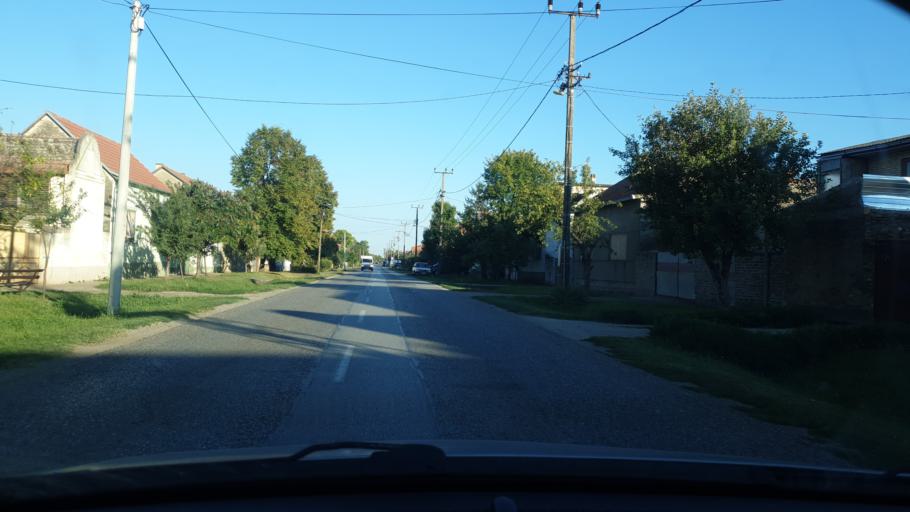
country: RS
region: Autonomna Pokrajina Vojvodina
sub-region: Sremski Okrug
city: Ruma
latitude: 44.9792
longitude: 19.8794
